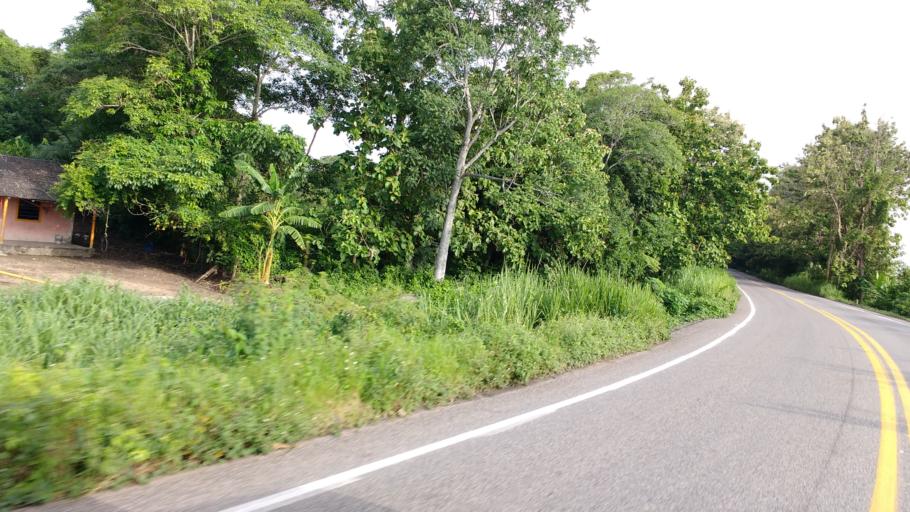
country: MX
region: Tabasco
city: Rio de Teapa
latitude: 17.6806
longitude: -92.9426
